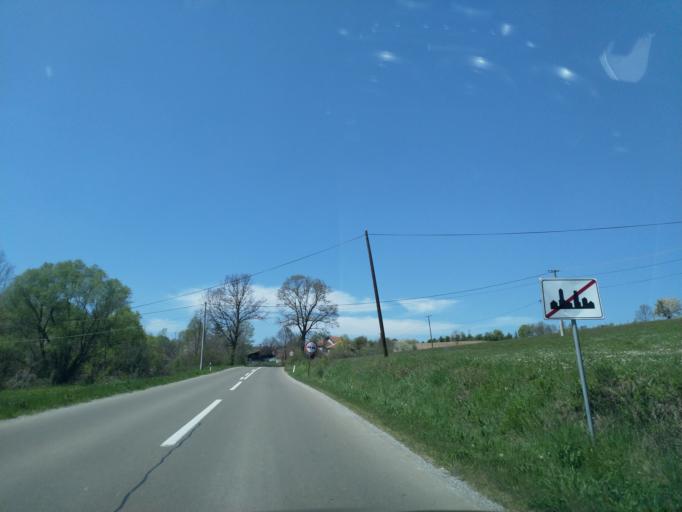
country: RS
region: Central Serbia
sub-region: Belgrade
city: Lazarevac
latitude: 44.3546
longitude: 20.3684
